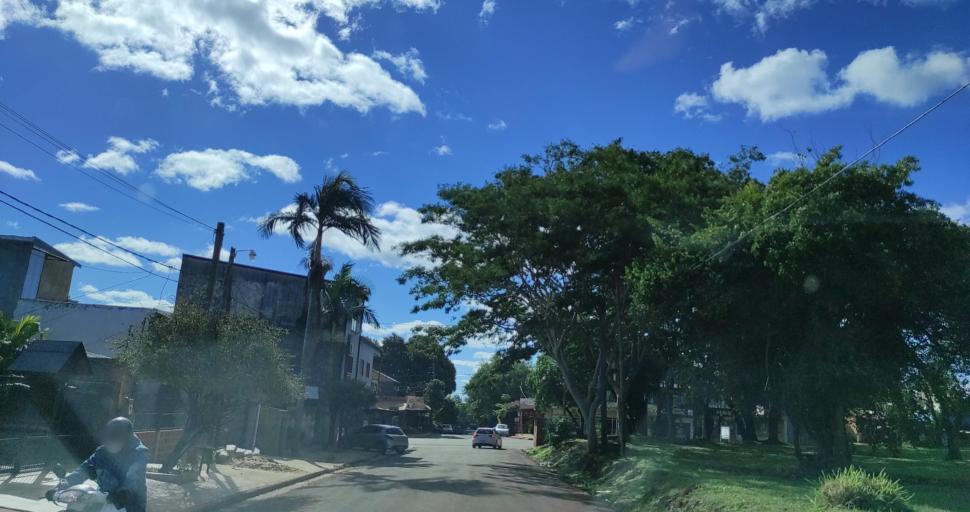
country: AR
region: Misiones
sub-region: Departamento de Capital
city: Posadas
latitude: -27.3675
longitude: -55.9342
